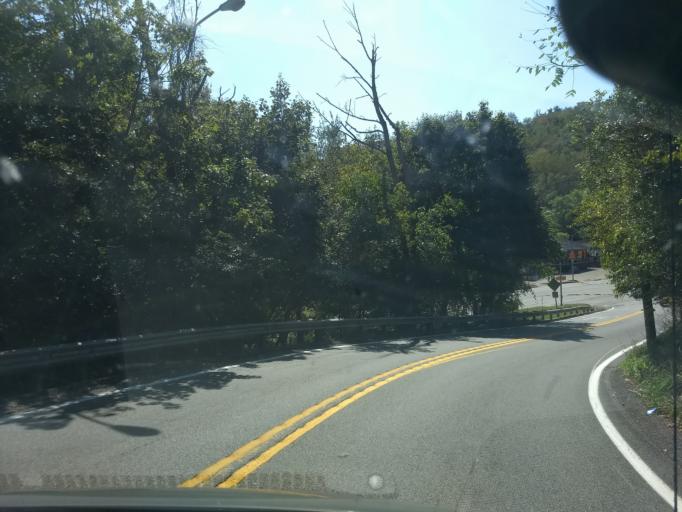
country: US
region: Pennsylvania
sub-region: Allegheny County
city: North Versailles
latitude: 40.3633
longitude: -79.8258
